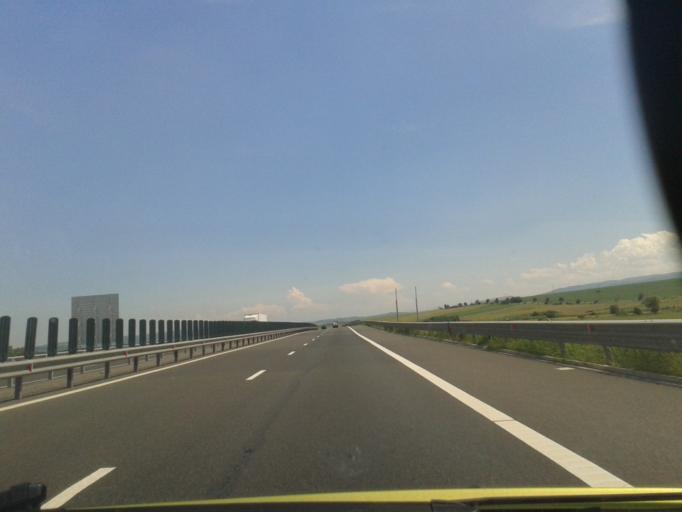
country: RO
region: Alba
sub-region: Comuna Garbova
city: Garbova
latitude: 45.9059
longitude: 23.7480
